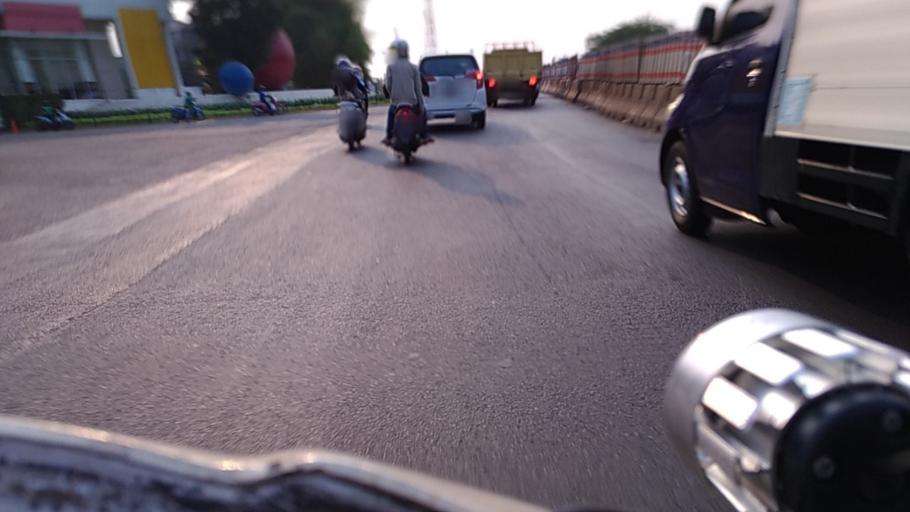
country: ID
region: West Java
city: Cileungsir
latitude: -6.3819
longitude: 106.9249
